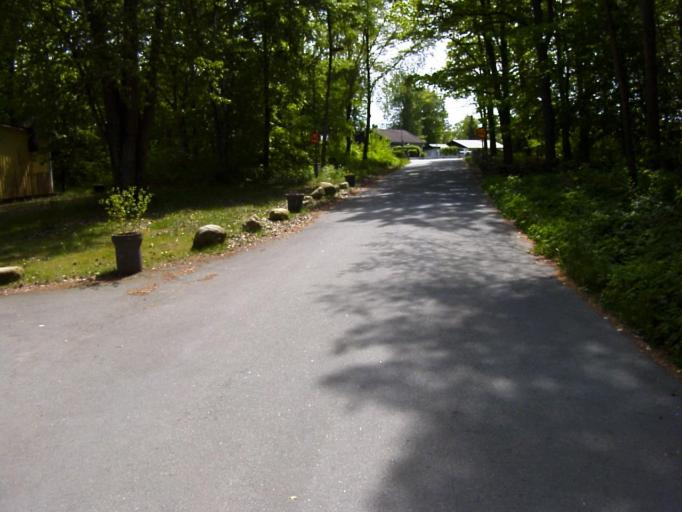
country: SE
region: Skane
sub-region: Kristianstads Kommun
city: Kristianstad
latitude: 56.0760
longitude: 14.0922
